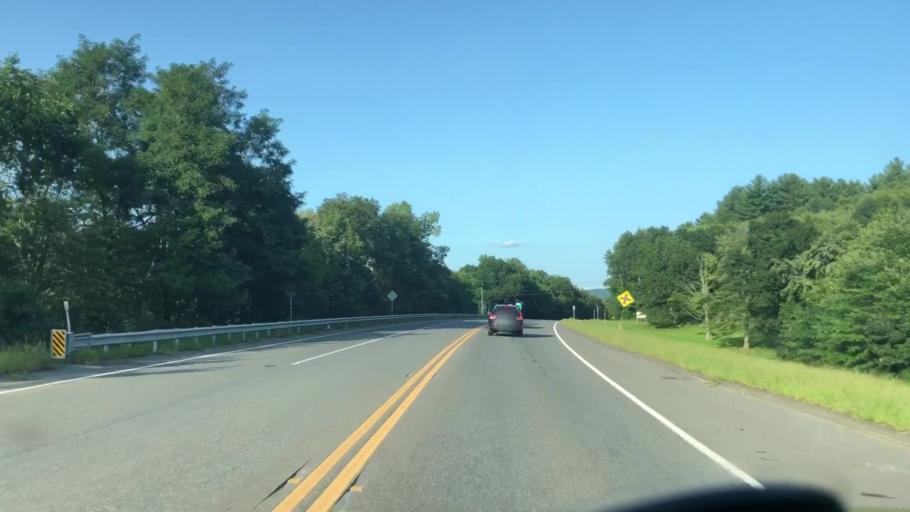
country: US
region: Massachusetts
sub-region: Franklin County
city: Gill
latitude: 42.6757
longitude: -72.4985
